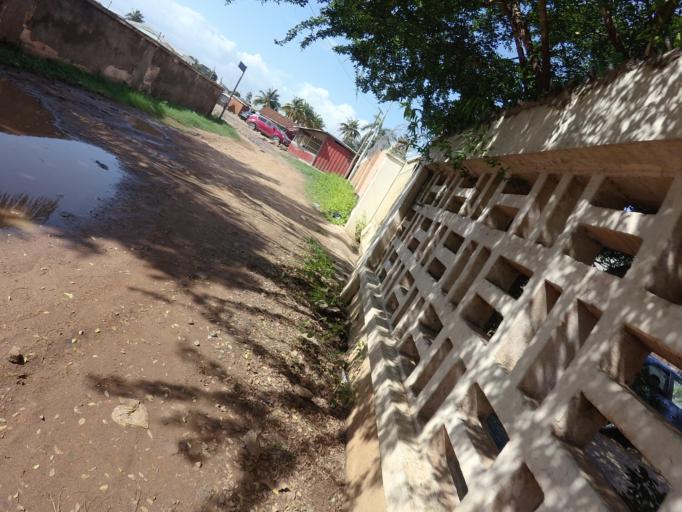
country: GH
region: Greater Accra
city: Accra
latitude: 5.5740
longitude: -0.2040
